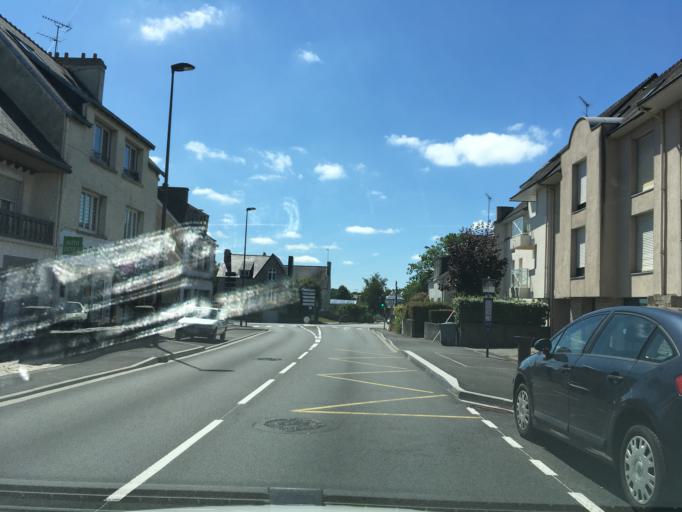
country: FR
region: Brittany
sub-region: Departement du Finistere
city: Quimper
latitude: 47.9882
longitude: -4.0988
